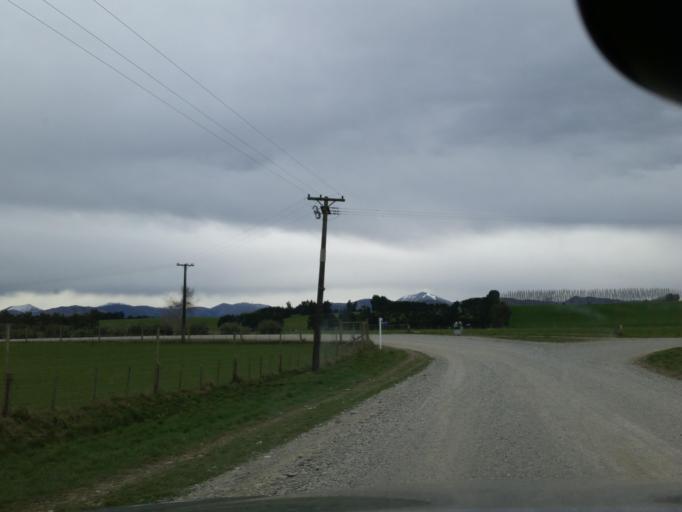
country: NZ
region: Southland
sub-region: Gore District
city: Gore
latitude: -45.8160
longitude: 168.7090
